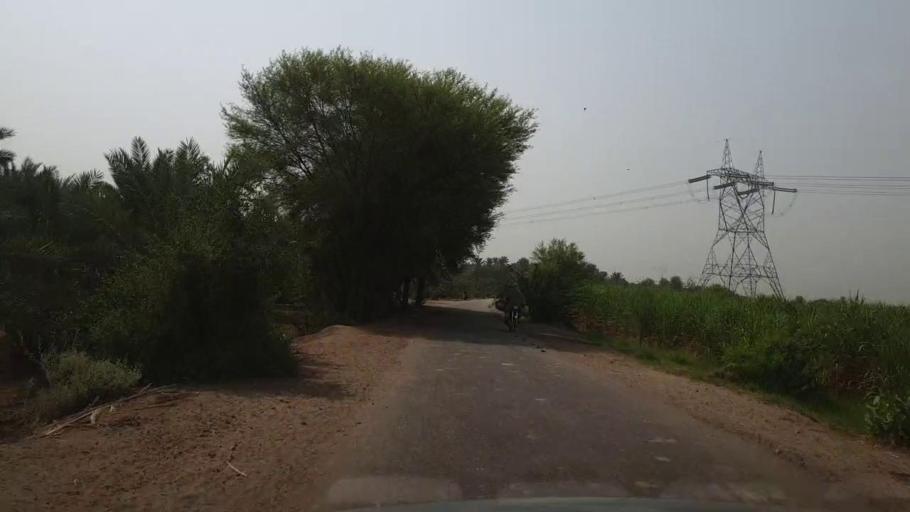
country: PK
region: Sindh
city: Gambat
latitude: 27.4142
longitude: 68.5533
